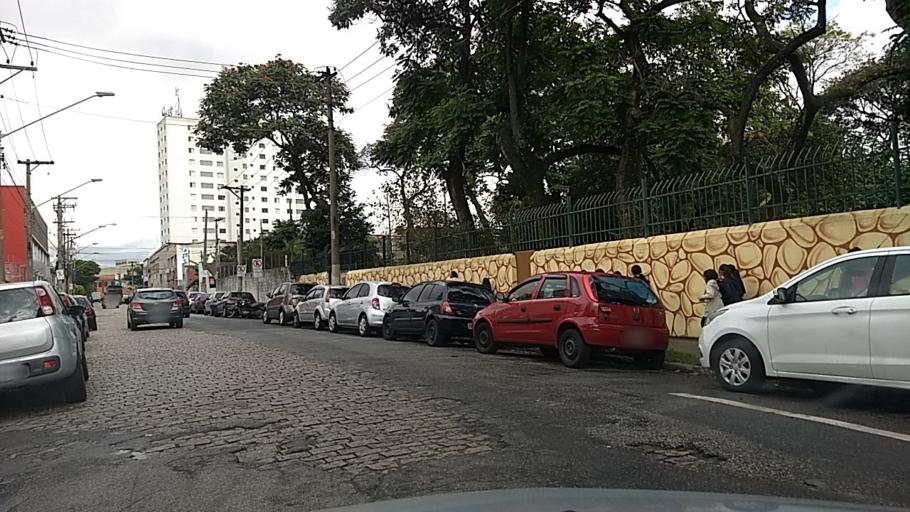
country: BR
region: Sao Paulo
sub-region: Sao Paulo
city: Sao Paulo
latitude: -23.5285
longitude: -46.6000
